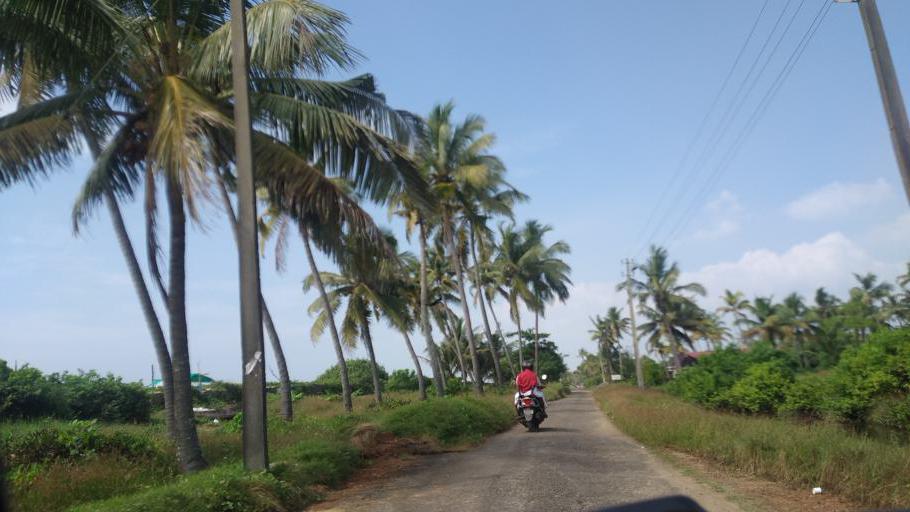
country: IN
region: Kerala
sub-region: Ernakulam
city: Elur
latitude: 10.0699
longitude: 76.1978
